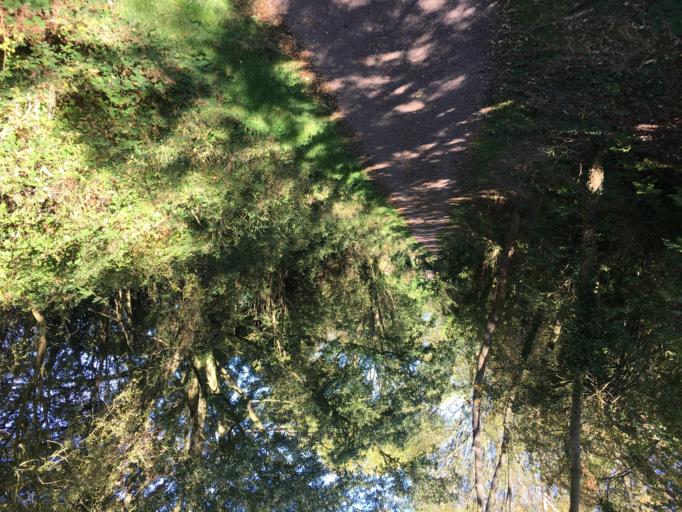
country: GB
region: England
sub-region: Warwickshire
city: Kenilworth
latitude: 52.3615
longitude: -1.5705
